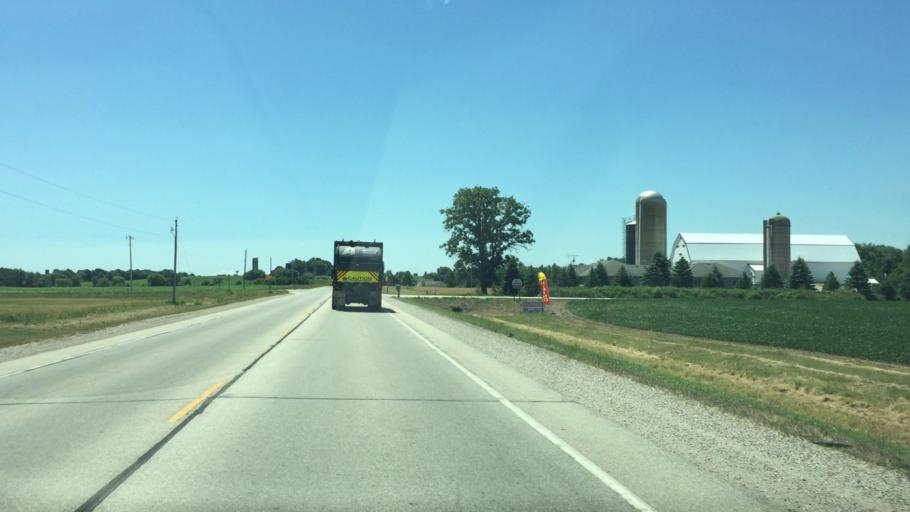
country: US
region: Wisconsin
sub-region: Calumet County
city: Chilton
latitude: 44.0671
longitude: -88.1632
